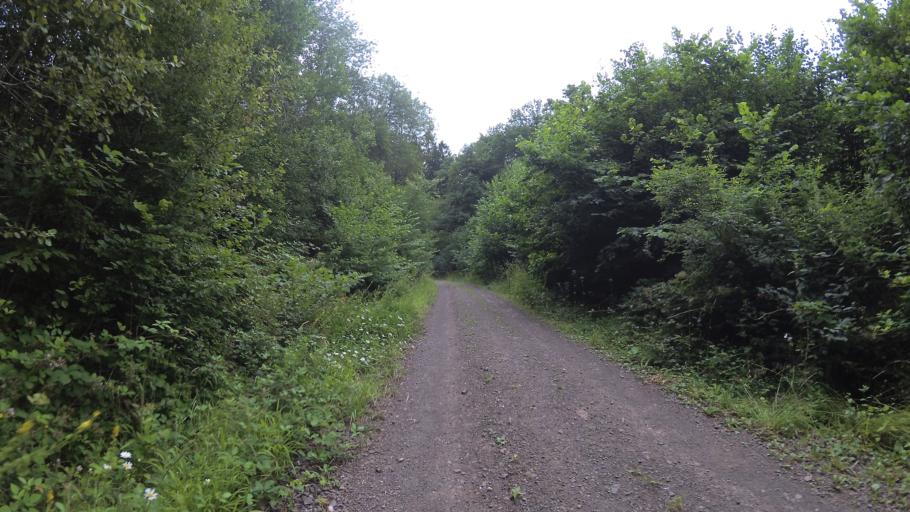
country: DE
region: Saarland
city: Mainzweiler
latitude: 49.4206
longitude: 7.1434
